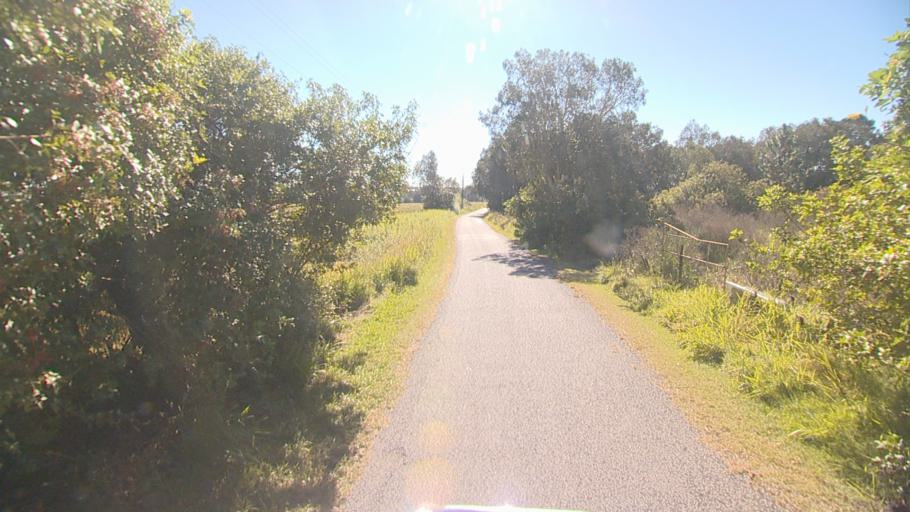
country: AU
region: Queensland
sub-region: Gold Coast
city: Yatala
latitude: -27.6860
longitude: 153.2246
